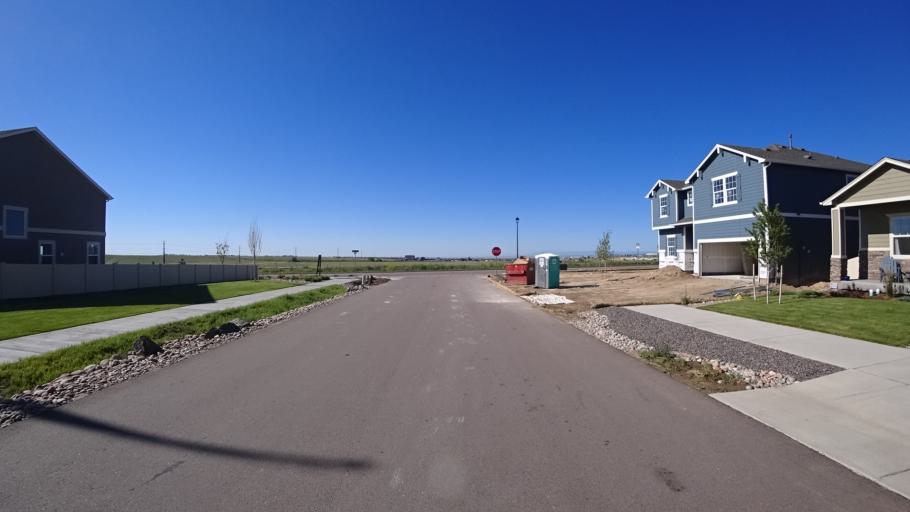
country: US
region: Colorado
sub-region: El Paso County
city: Cimarron Hills
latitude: 38.8942
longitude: -104.6773
